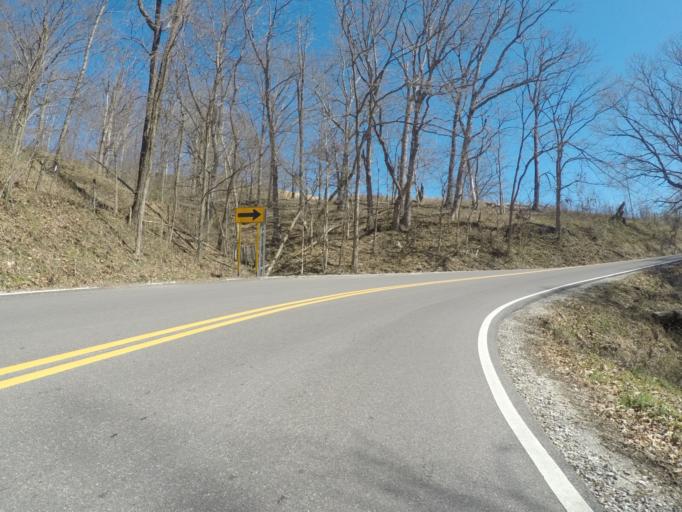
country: US
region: Ohio
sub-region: Lawrence County
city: South Point
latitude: 38.4586
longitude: -82.5527
